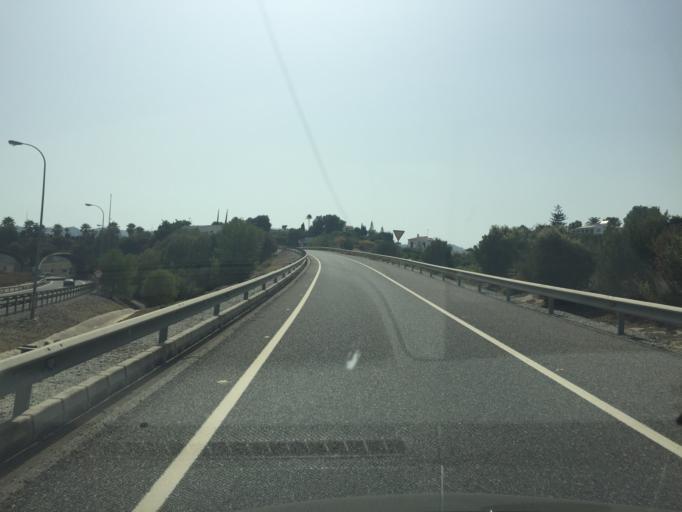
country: ES
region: Andalusia
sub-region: Provincia de Malaga
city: Nerja
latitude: 36.7641
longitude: -3.8857
